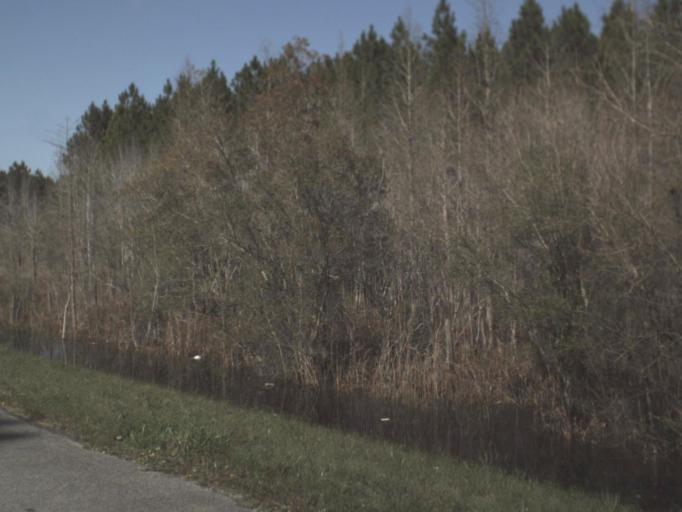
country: US
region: Florida
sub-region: Gulf County
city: Wewahitchka
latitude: 30.0184
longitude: -85.1778
